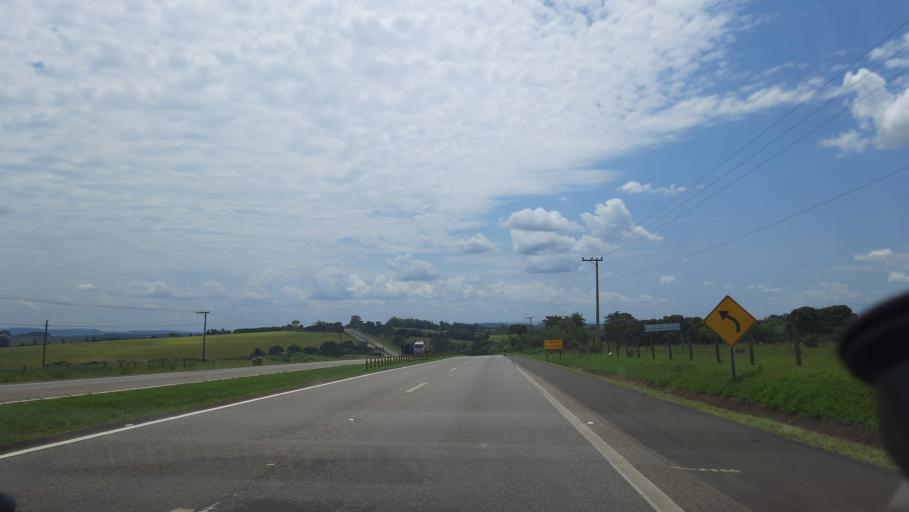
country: BR
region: Sao Paulo
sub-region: Casa Branca
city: Casa Branca
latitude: -21.7375
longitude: -47.0734
